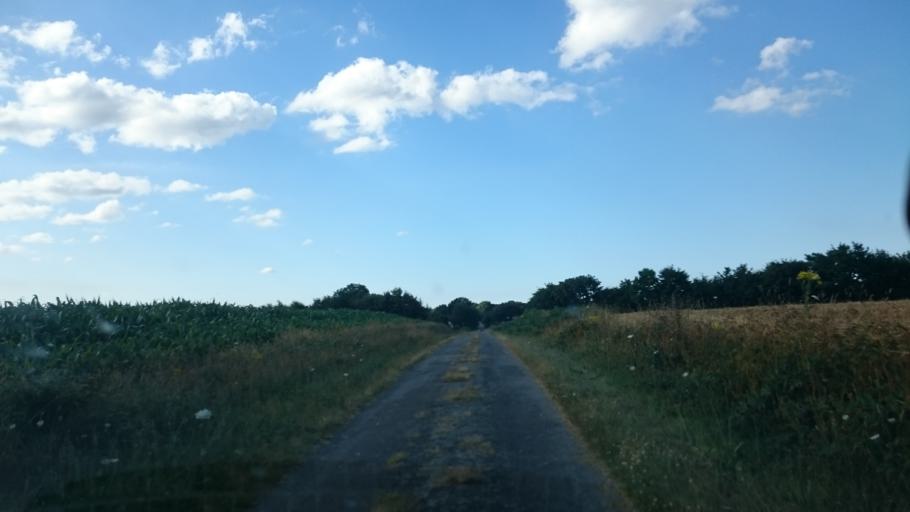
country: FR
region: Brittany
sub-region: Departement d'Ille-et-Vilaine
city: Crevin
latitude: 47.9332
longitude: -1.6458
